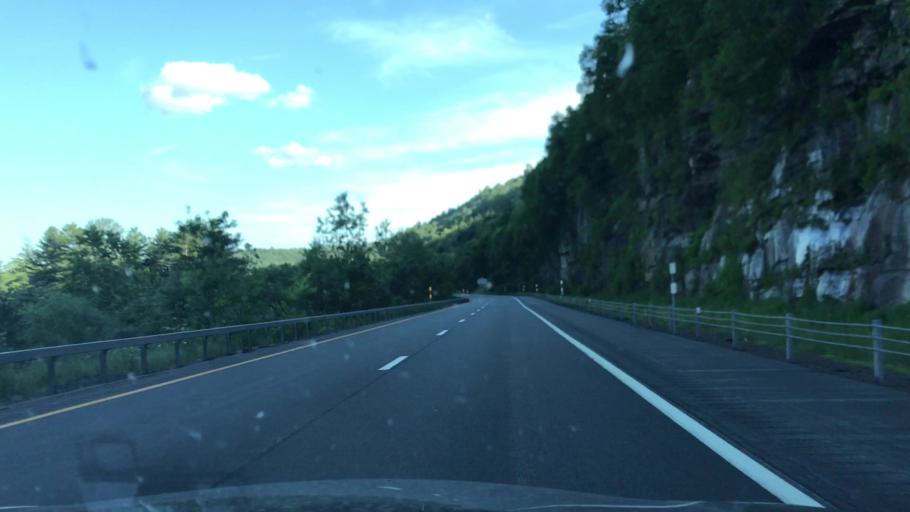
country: US
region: New York
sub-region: Sullivan County
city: Livingston Manor
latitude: 41.9478
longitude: -74.9322
